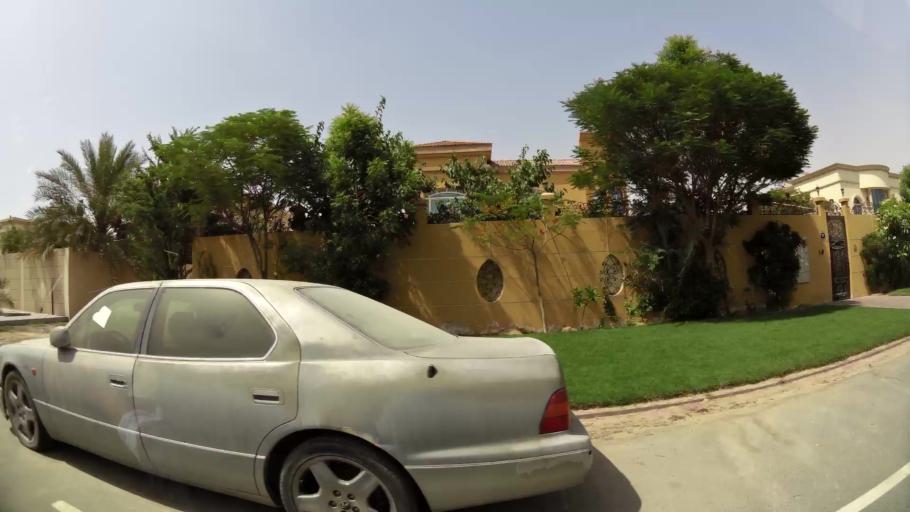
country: AE
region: Ash Shariqah
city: Sharjah
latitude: 25.2393
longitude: 55.4305
